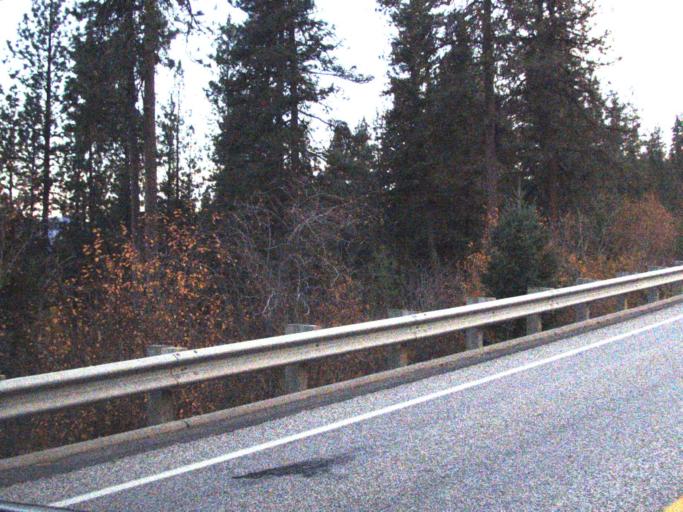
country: US
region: Washington
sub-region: Stevens County
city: Kettle Falls
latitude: 48.6173
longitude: -118.1375
